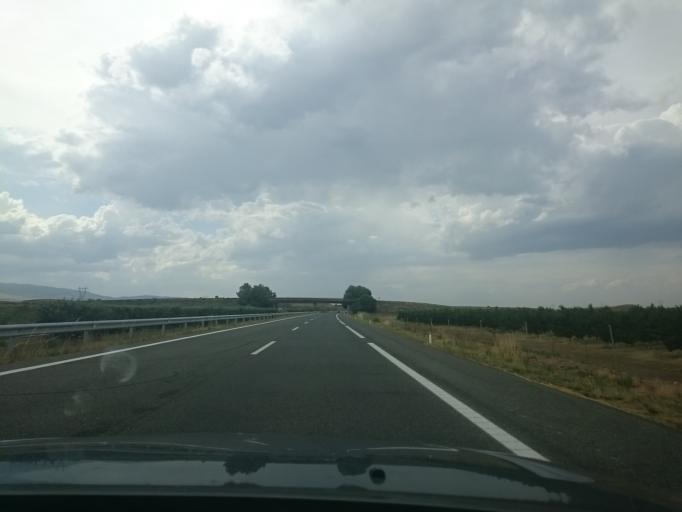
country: ES
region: Navarre
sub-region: Provincia de Navarra
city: Corella
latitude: 42.1553
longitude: -1.8108
